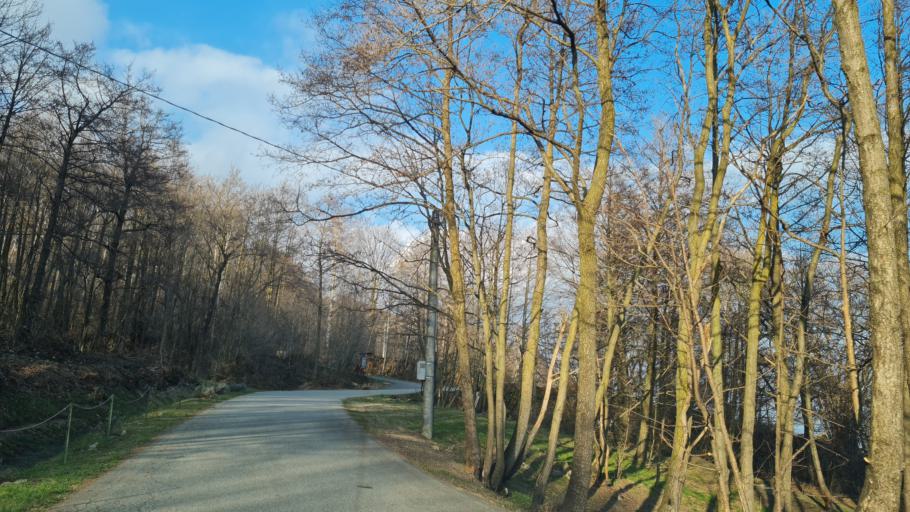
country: IT
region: Piedmont
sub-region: Provincia di Biella
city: Donato
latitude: 45.5463
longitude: 7.9158
